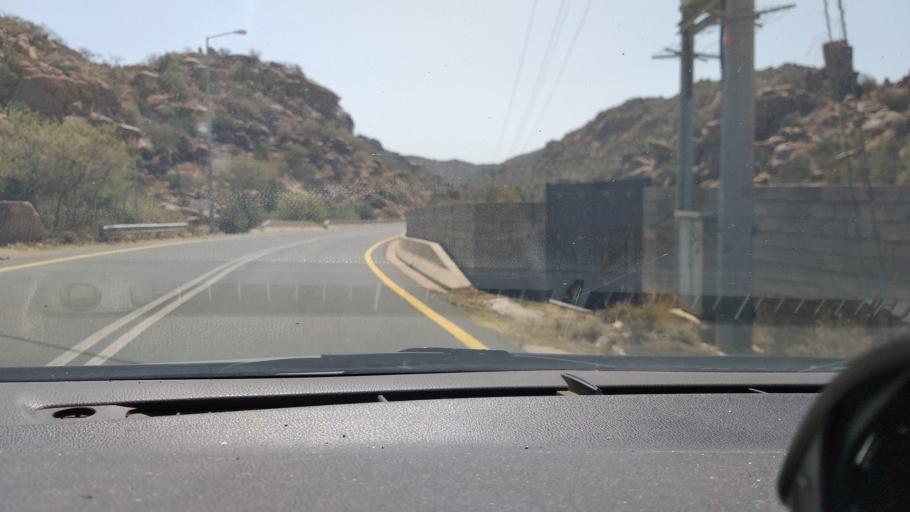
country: SA
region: Makkah
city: Ash Shafa
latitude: 21.0922
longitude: 40.3719
